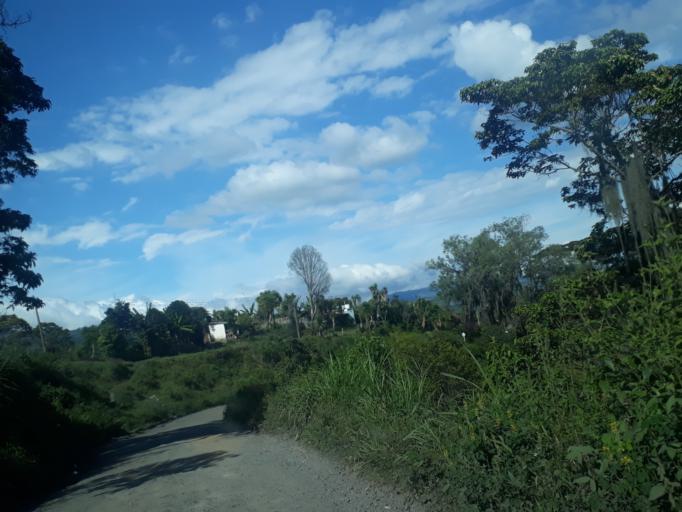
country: CO
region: Santander
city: Velez
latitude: 6.0417
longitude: -73.6533
